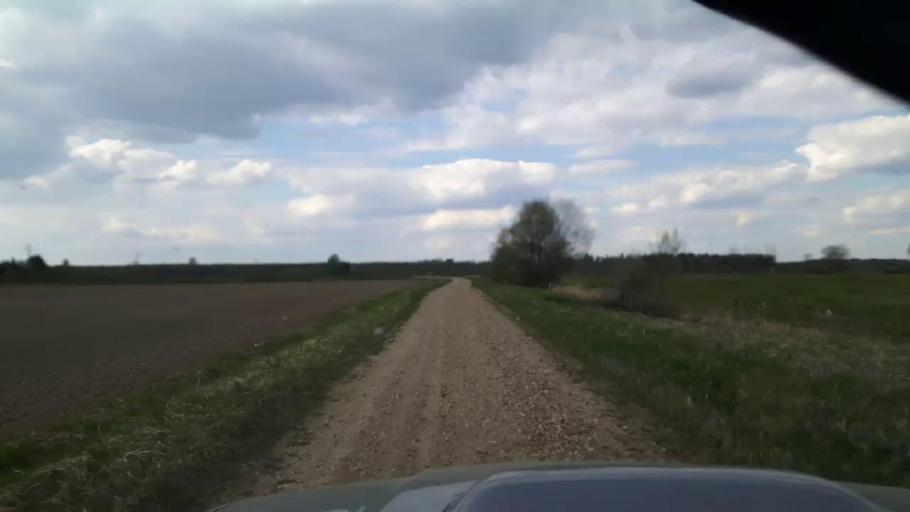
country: EE
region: Paernumaa
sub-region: Sindi linn
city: Sindi
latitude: 58.4356
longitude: 24.7492
